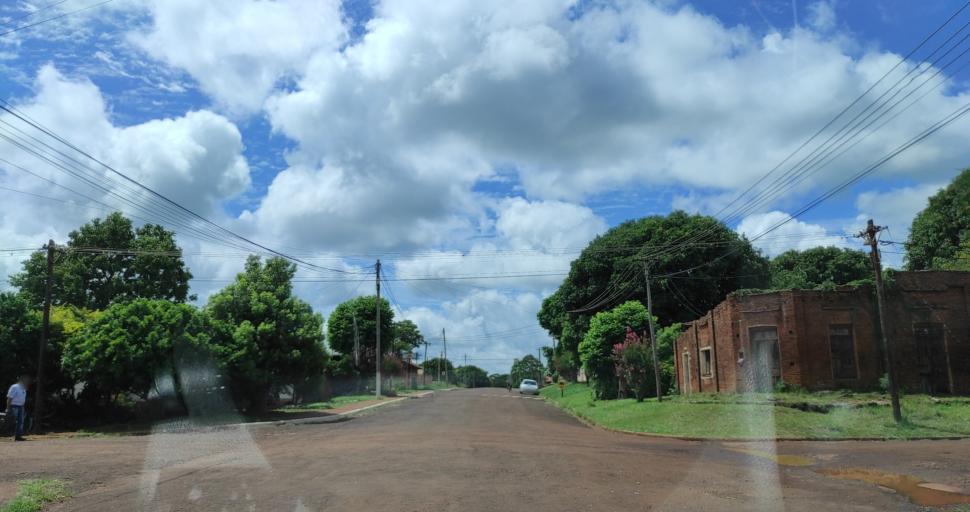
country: AR
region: Misiones
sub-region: Departamento de Apostoles
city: San Jose
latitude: -27.7685
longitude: -55.7751
